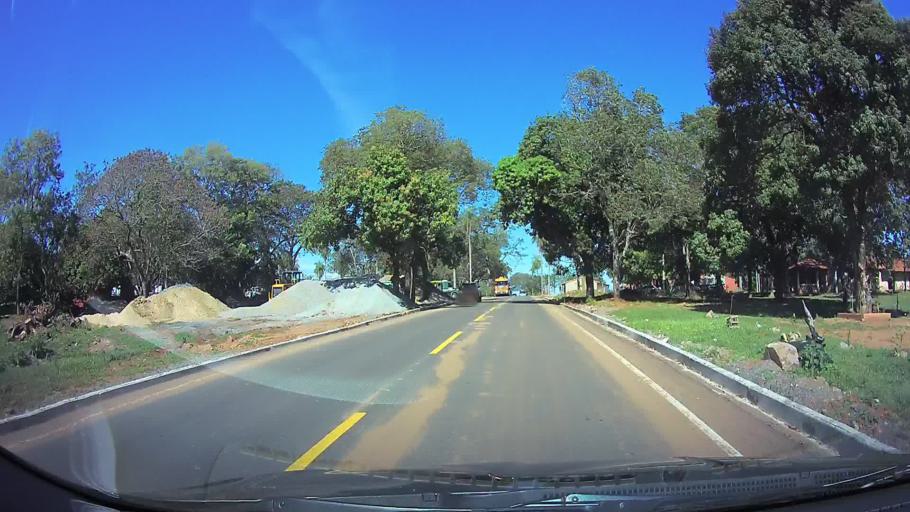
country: PY
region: Central
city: Limpio
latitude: -25.2541
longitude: -57.4644
